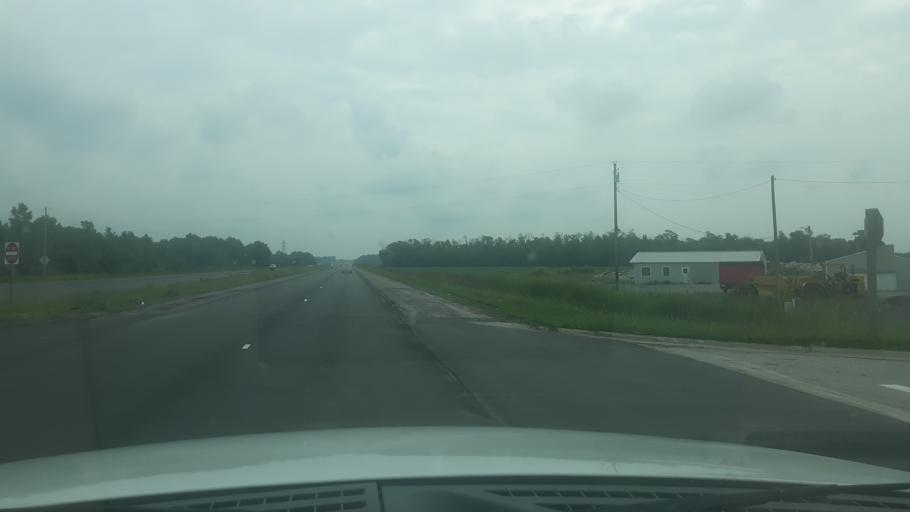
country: US
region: Illinois
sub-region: Saline County
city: Harrisburg
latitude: 37.7711
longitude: -88.5089
